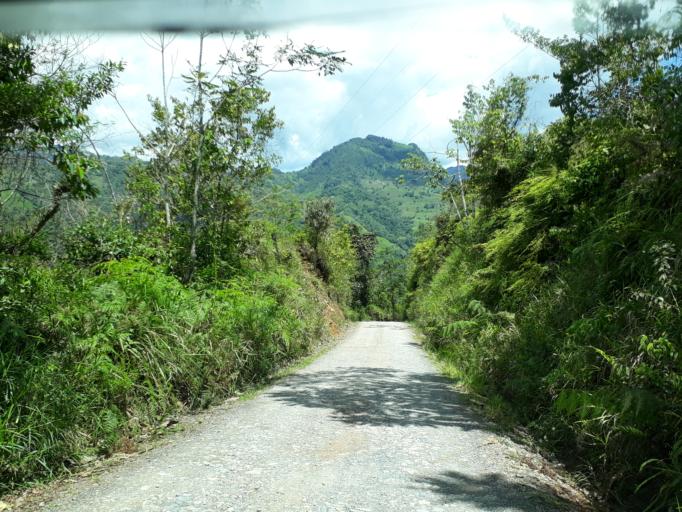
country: CO
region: Cundinamarca
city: Topaipi
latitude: 5.3554
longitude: -74.1953
